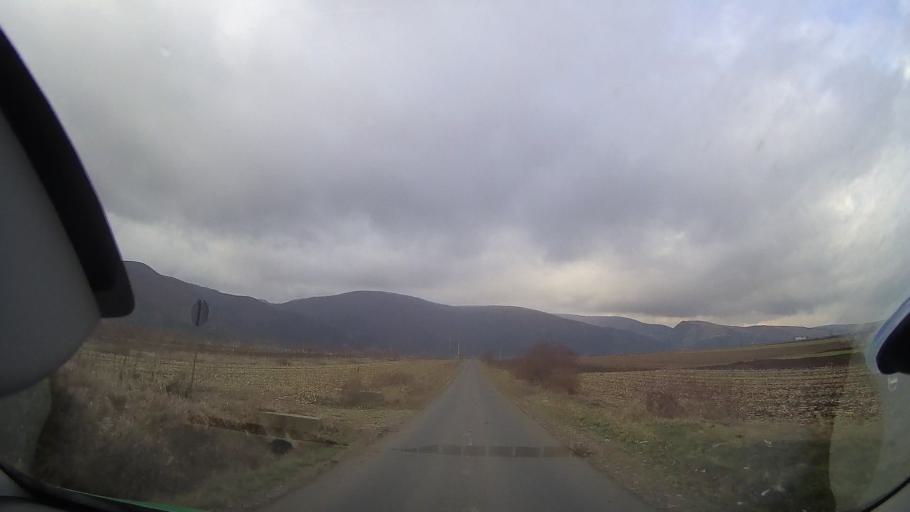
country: RO
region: Cluj
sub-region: Comuna Moldovenesti
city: Moldovenesti
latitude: 46.5048
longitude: 23.6748
